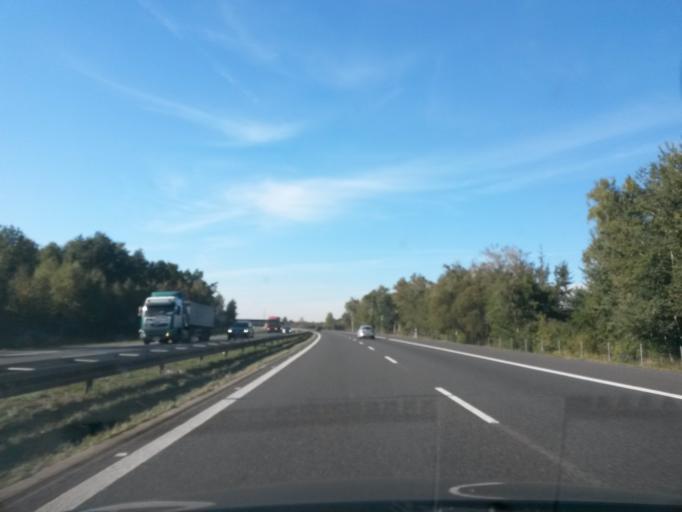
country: PL
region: Opole Voivodeship
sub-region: Powiat brzeski
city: Lewin Brzeski
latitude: 50.7028
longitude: 17.6167
